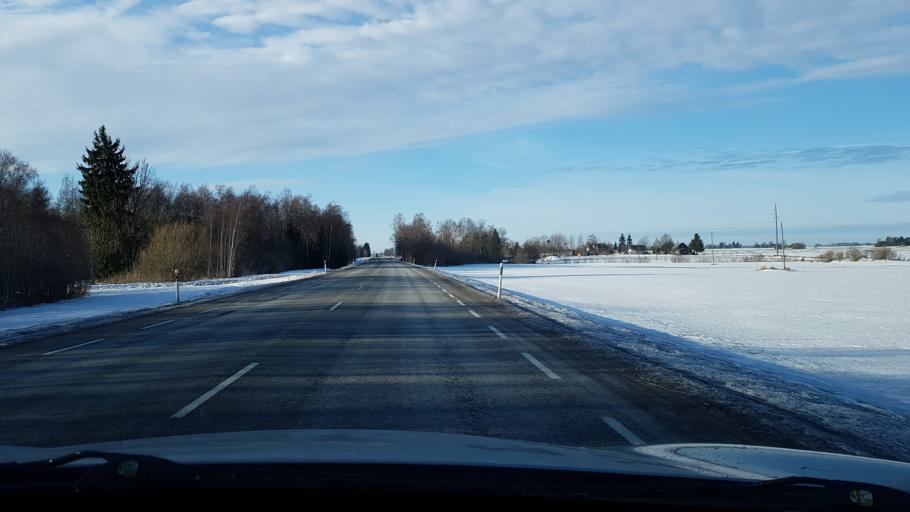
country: EE
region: Viljandimaa
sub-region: Vohma linn
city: Vohma
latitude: 58.6656
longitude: 25.6298
